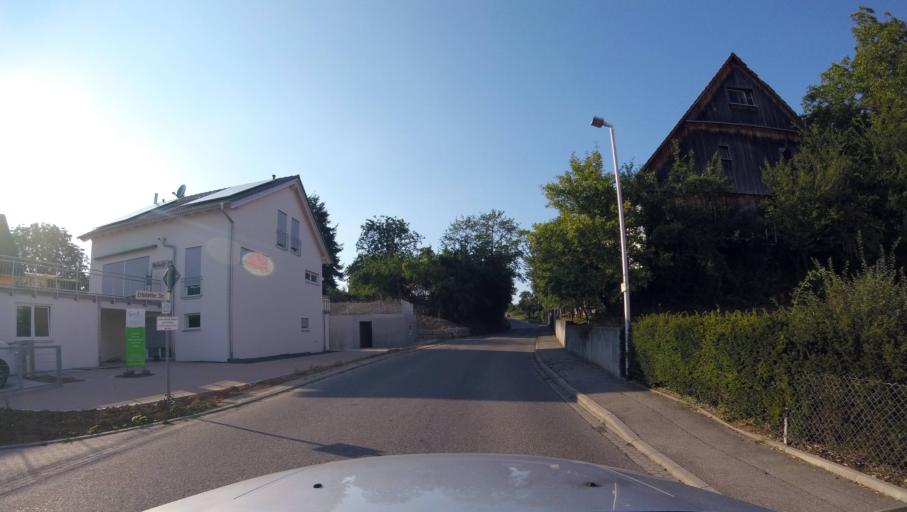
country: DE
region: Baden-Wuerttemberg
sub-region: Regierungsbezirk Stuttgart
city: Leutenbach
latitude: 48.9014
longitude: 9.4021
